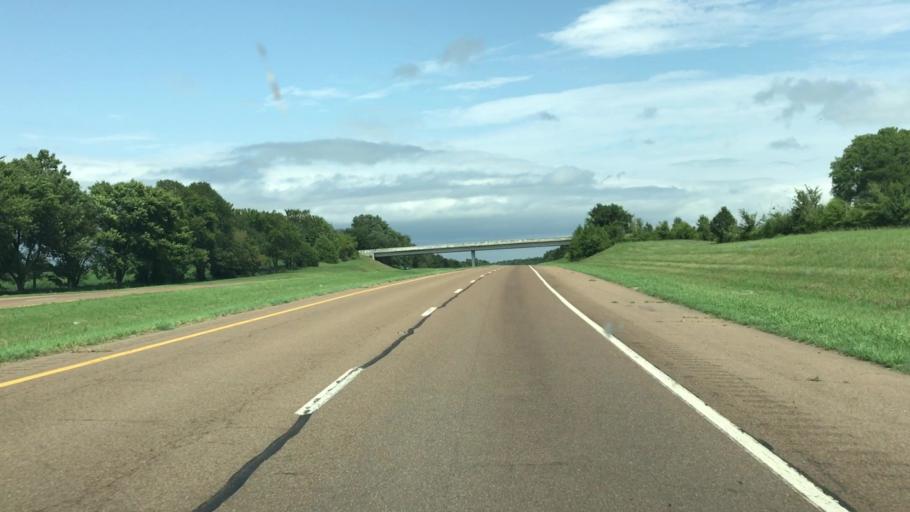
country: US
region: Tennessee
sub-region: Obion County
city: South Fulton
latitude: 36.4753
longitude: -88.9591
